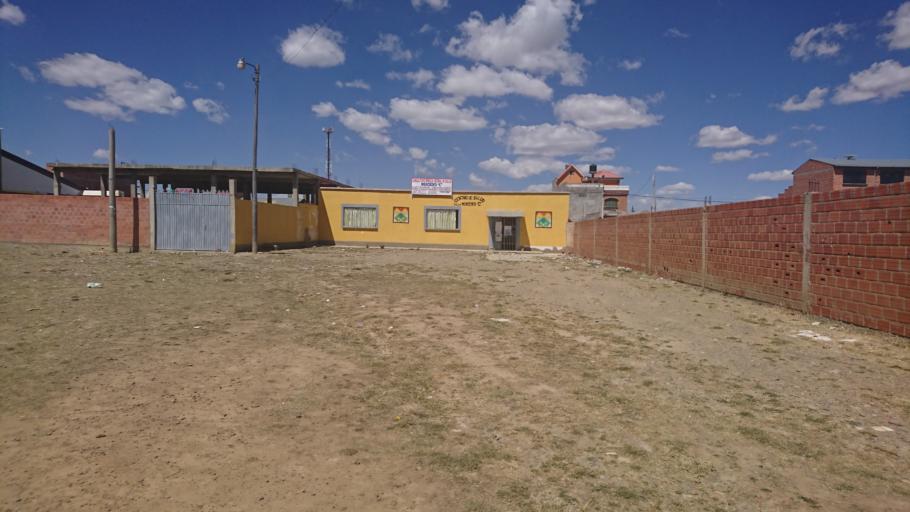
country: BO
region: La Paz
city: La Paz
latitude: -16.5646
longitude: -68.2148
